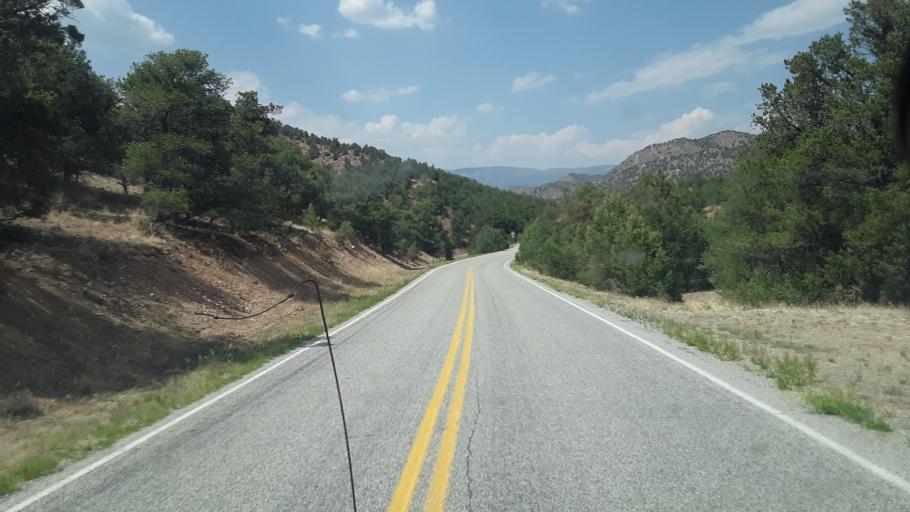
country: US
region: Colorado
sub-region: Custer County
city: Westcliffe
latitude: 38.3788
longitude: -105.5830
